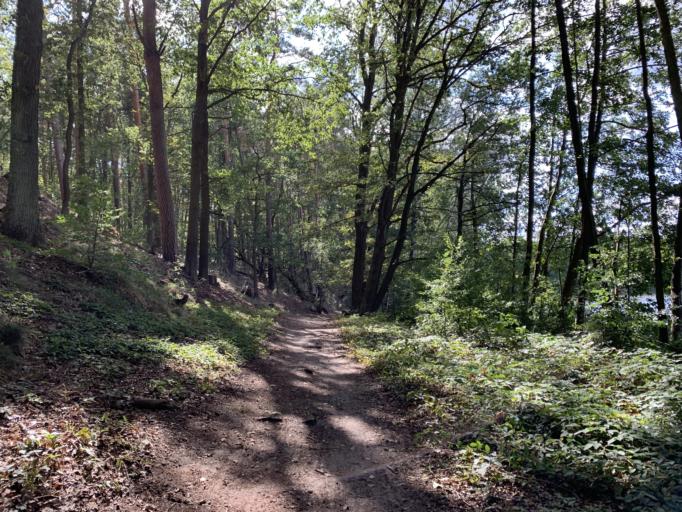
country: DE
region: Brandenburg
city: Michendorf
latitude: 52.3136
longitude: 12.9834
